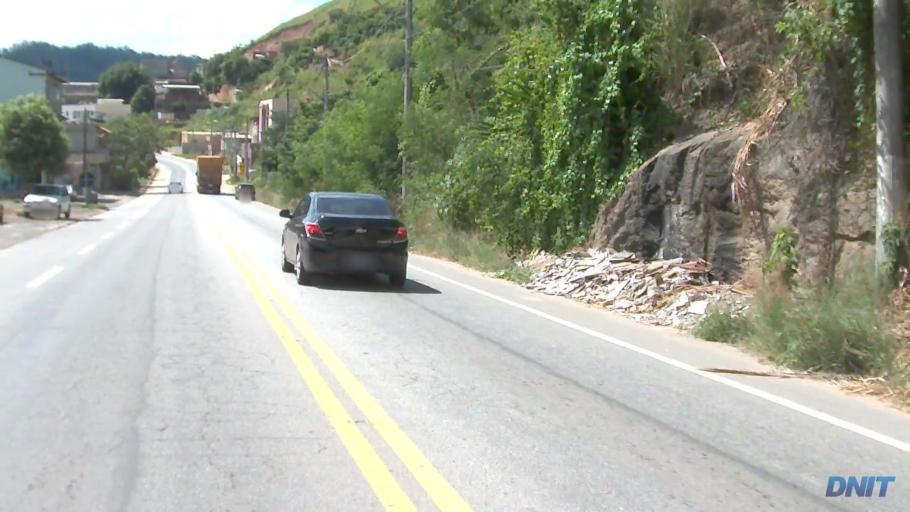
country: BR
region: Minas Gerais
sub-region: Coronel Fabriciano
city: Coronel Fabriciano
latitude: -19.5375
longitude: -42.6700
